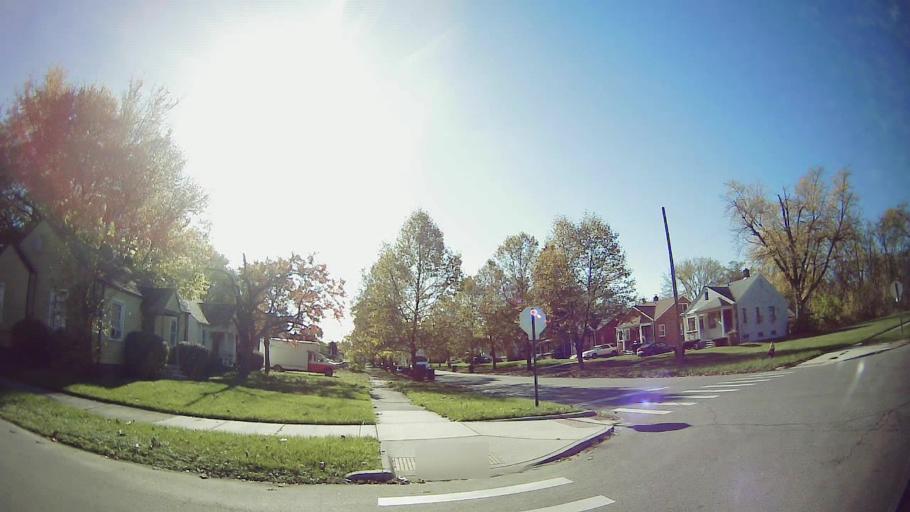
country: US
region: Michigan
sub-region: Wayne County
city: Redford
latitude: 42.3889
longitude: -83.2304
